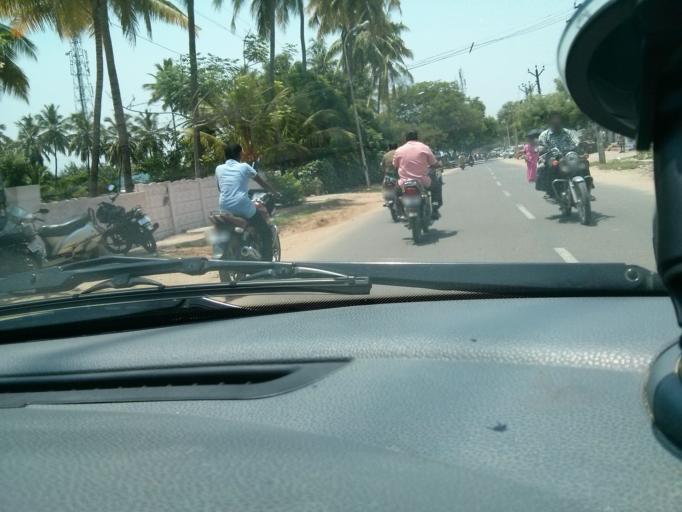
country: IN
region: Tamil Nadu
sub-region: Coimbatore
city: Coimbatore
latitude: 11.0344
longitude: 76.9636
